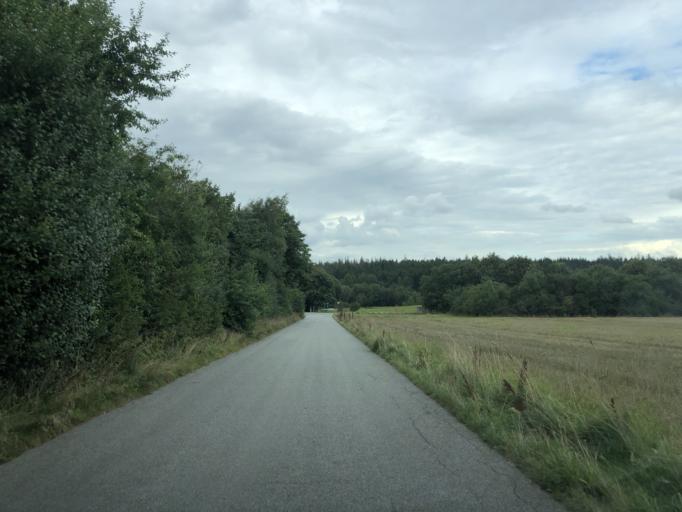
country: DK
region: Central Jutland
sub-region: Holstebro Kommune
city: Ulfborg
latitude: 56.2001
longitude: 8.4238
